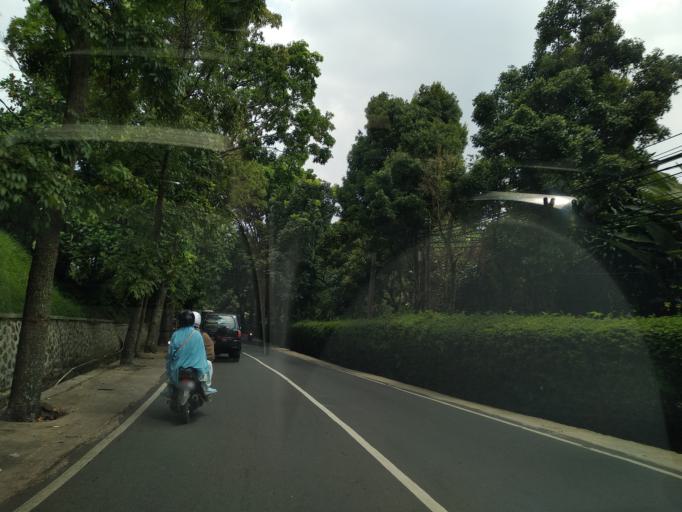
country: ID
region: West Java
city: Lembang
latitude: -6.8491
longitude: 107.5972
